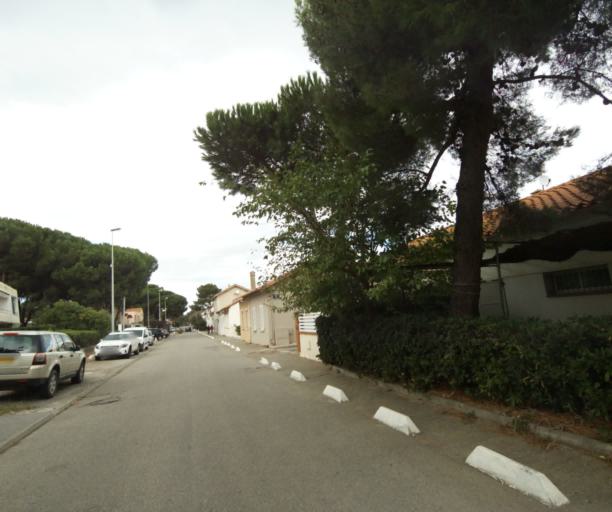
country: FR
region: Languedoc-Roussillon
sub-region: Departement des Pyrenees-Orientales
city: Collioure
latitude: 42.5366
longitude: 3.0556
